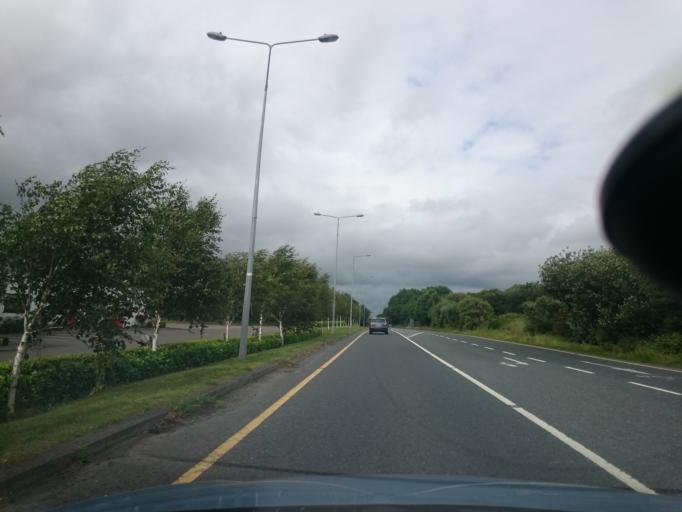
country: IE
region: Leinster
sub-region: County Carlow
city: Carlow
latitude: 52.8593
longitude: -6.8768
